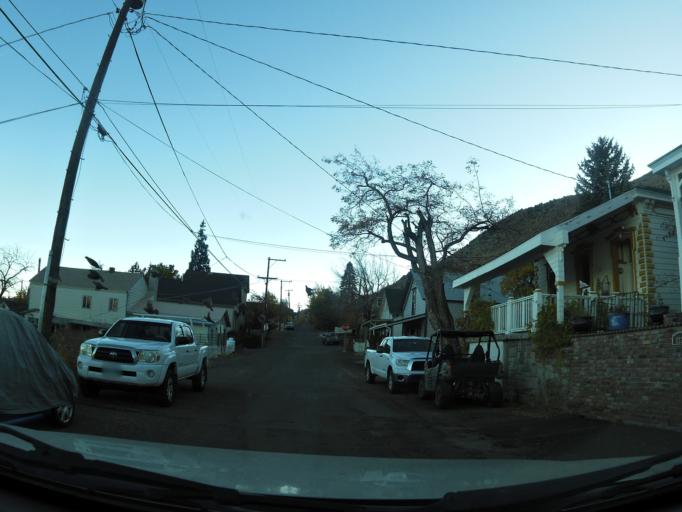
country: US
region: Nevada
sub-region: Storey County
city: Virginia City
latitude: 39.3129
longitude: -119.6500
